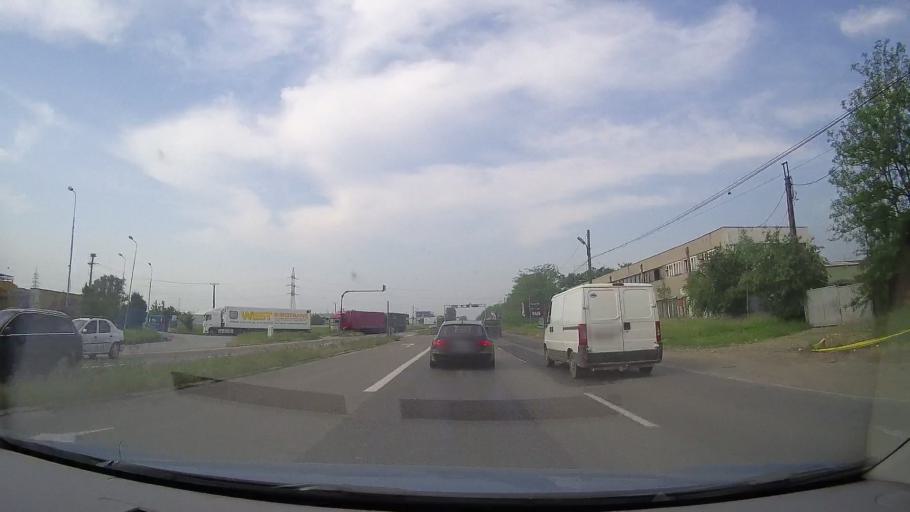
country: RO
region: Timis
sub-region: Comuna Giroc
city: Chisoda
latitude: 45.7119
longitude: 21.1914
